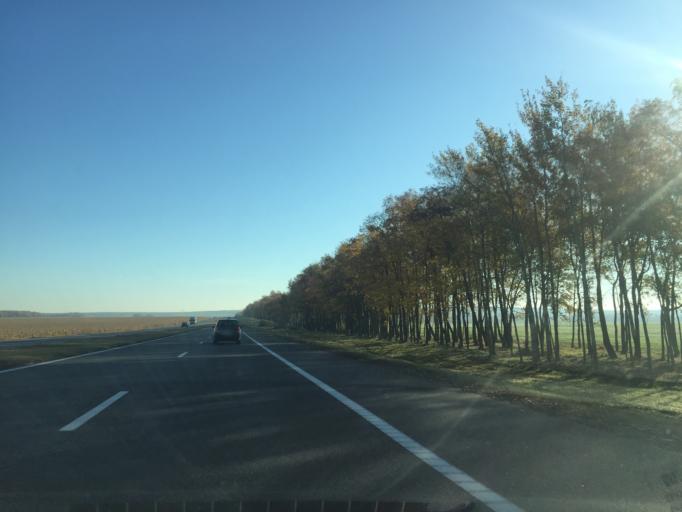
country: BY
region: Minsk
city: Smilavichy
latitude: 53.7615
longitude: 28.0598
